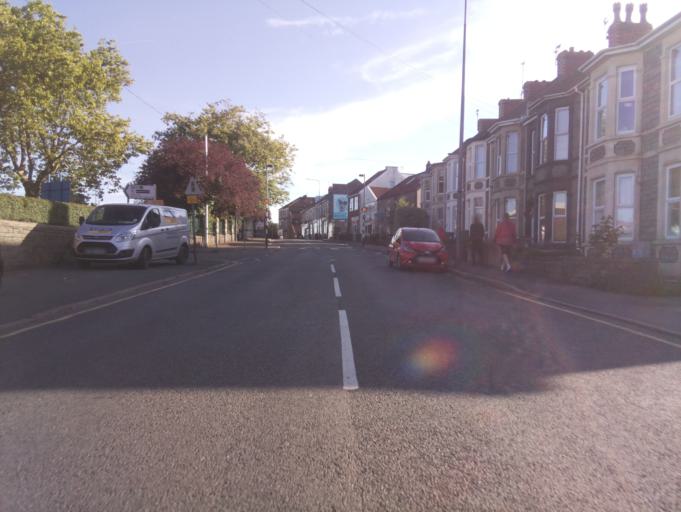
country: GB
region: England
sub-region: South Gloucestershire
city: Mangotsfield
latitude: 51.4798
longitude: -2.5071
